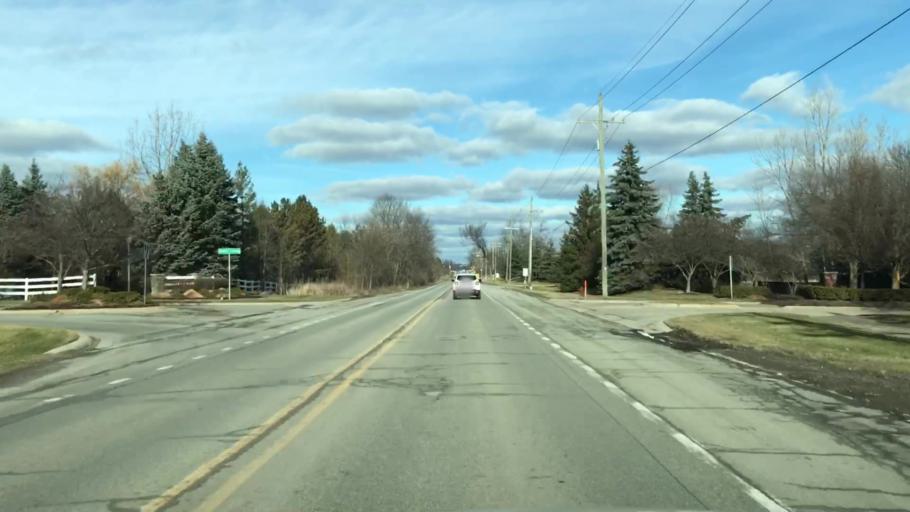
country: US
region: Michigan
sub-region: Oakland County
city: Auburn Hills
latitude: 42.7337
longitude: -83.1966
